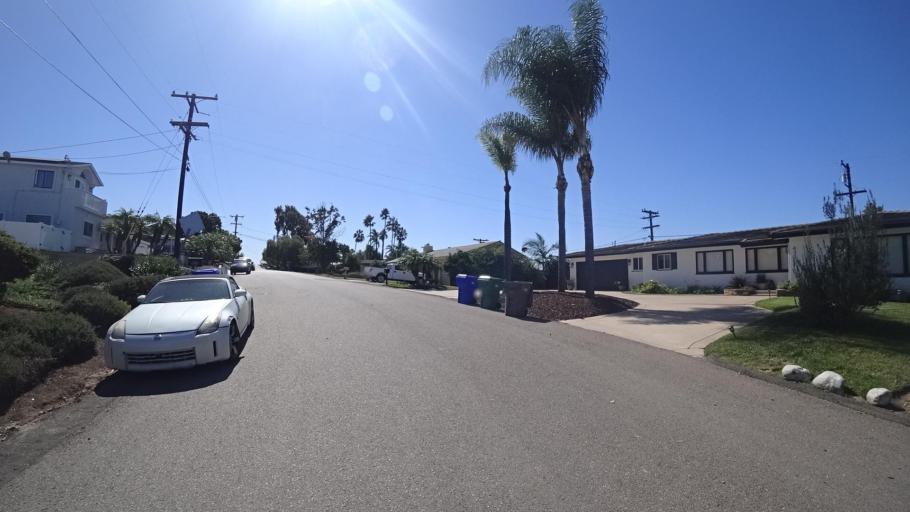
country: US
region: California
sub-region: San Diego County
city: Bonita
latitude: 32.6464
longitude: -117.0509
